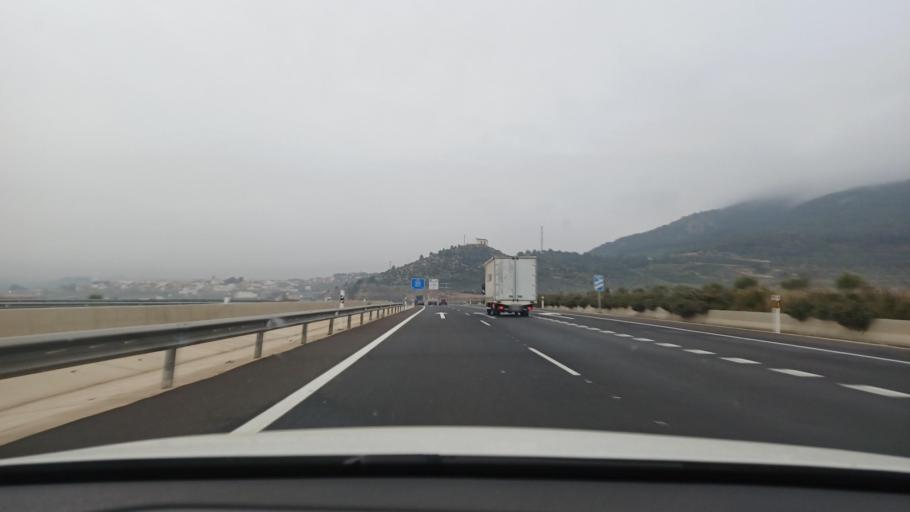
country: ES
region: Valencia
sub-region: Provincia de Valencia
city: La Font de la Figuera
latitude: 38.8206
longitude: -0.8907
